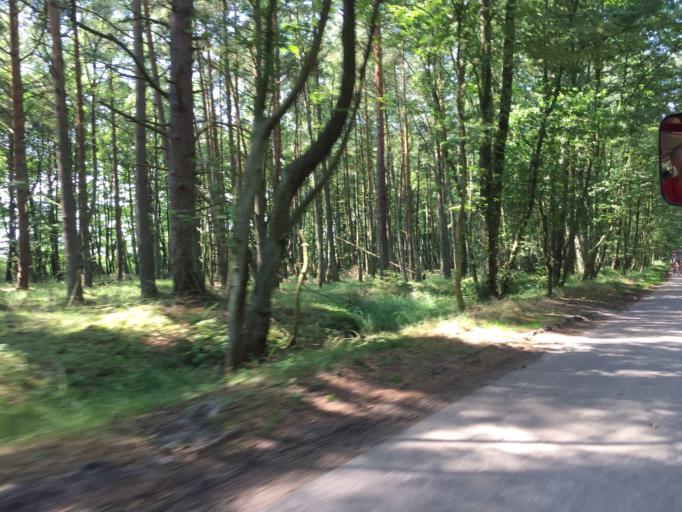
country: PL
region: Pomeranian Voivodeship
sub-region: Powiat leborski
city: Leba
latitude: 54.7526
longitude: 17.4880
